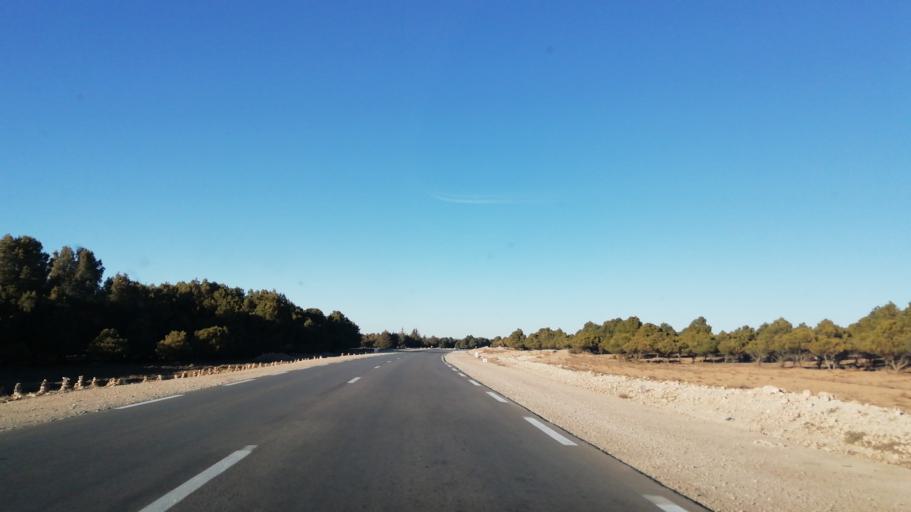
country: DZ
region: Tlemcen
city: Sebdou
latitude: 34.4565
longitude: -1.2755
